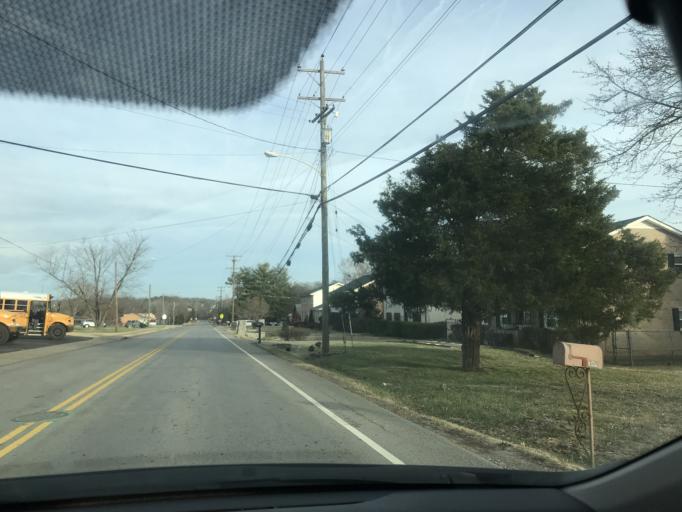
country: US
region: Tennessee
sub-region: Davidson County
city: Nashville
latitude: 36.2197
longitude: -86.8280
